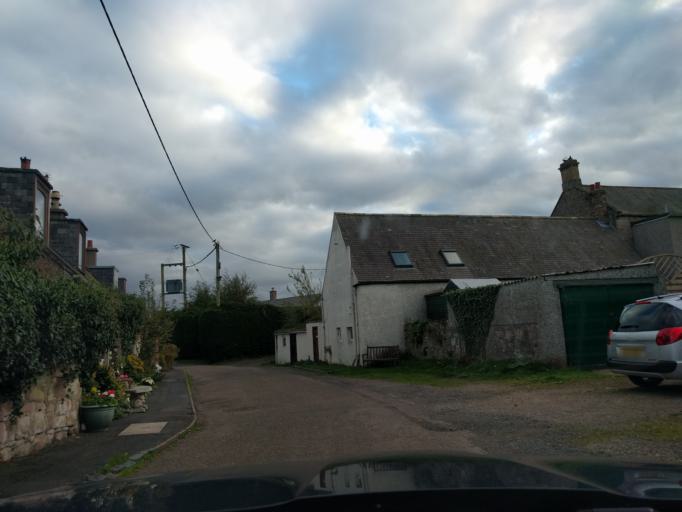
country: GB
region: Scotland
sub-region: The Scottish Borders
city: Allanton
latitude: 55.7406
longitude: -2.1151
